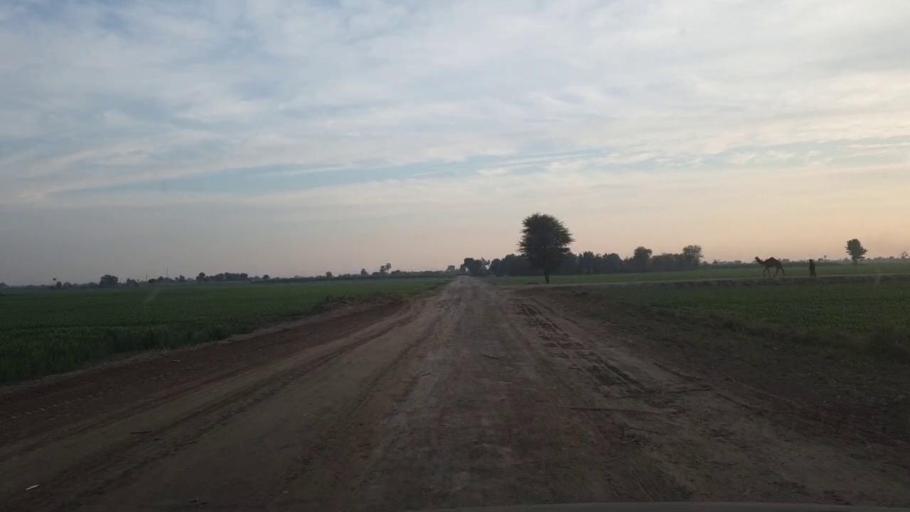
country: PK
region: Sindh
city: Shahpur Chakar
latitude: 26.0551
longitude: 68.5323
